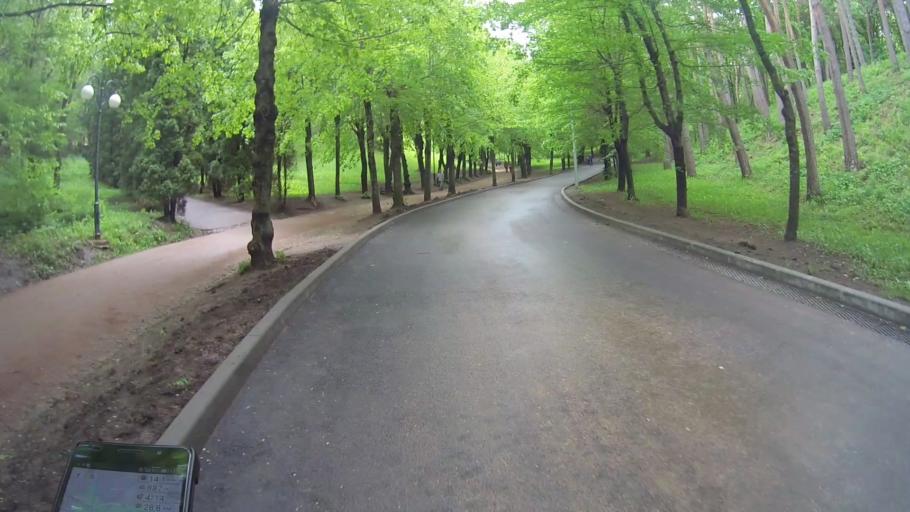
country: RU
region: Stavropol'skiy
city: Kislovodsk
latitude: 43.8970
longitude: 42.7274
